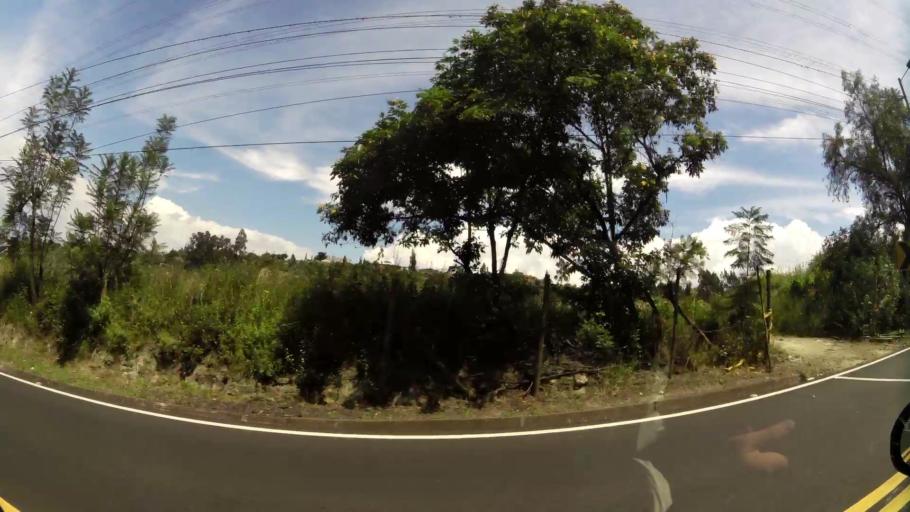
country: EC
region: Pichincha
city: Sangolqui
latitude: -0.2036
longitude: -78.3701
